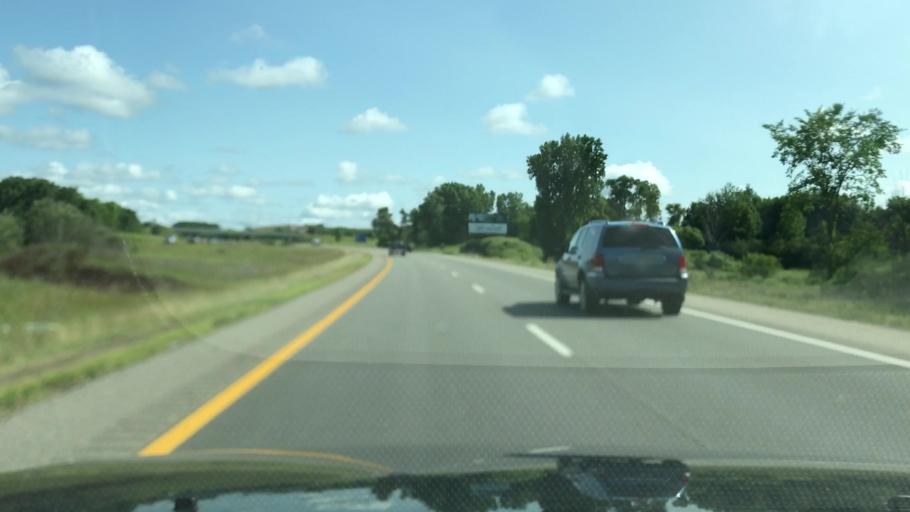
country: US
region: Michigan
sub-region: Montcalm County
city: Howard City
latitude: 43.3180
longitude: -85.5179
